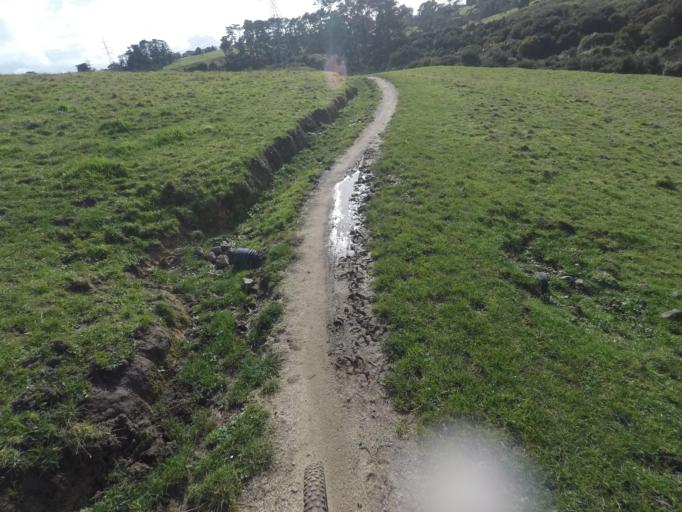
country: NZ
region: Auckland
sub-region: Auckland
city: Manukau City
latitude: -36.9963
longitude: 174.9097
